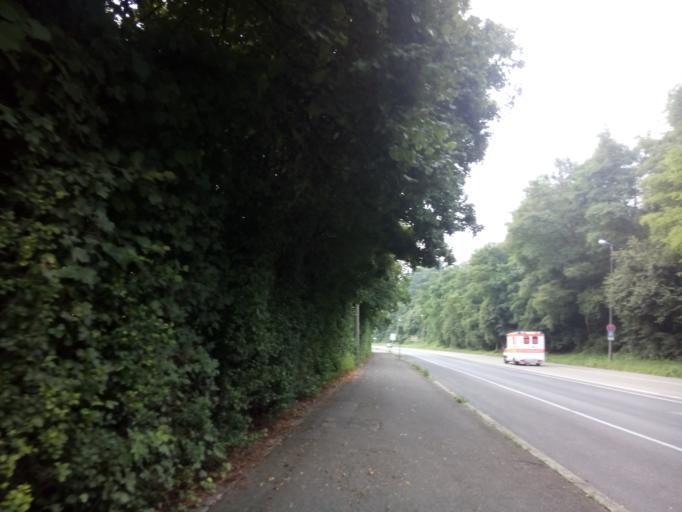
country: DE
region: Baden-Wuerttemberg
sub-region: Tuebingen Region
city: Tuebingen
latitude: 48.5314
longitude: 9.0436
